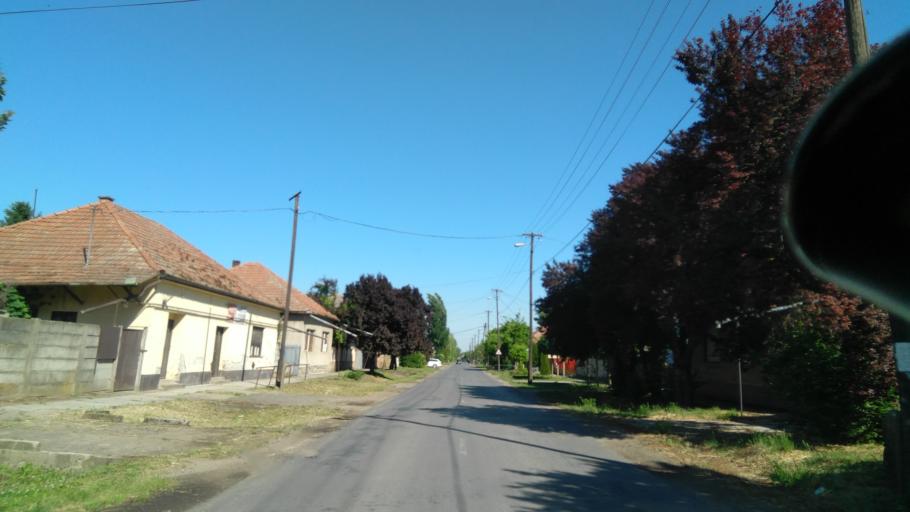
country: HU
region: Bekes
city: Kevermes
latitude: 46.4170
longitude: 21.1799
